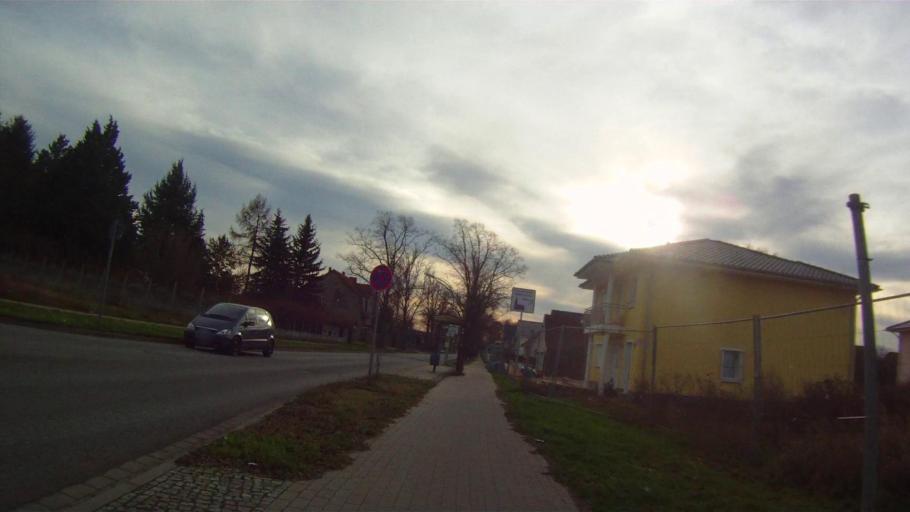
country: DE
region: Berlin
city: Buckow
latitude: 52.4143
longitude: 13.4388
